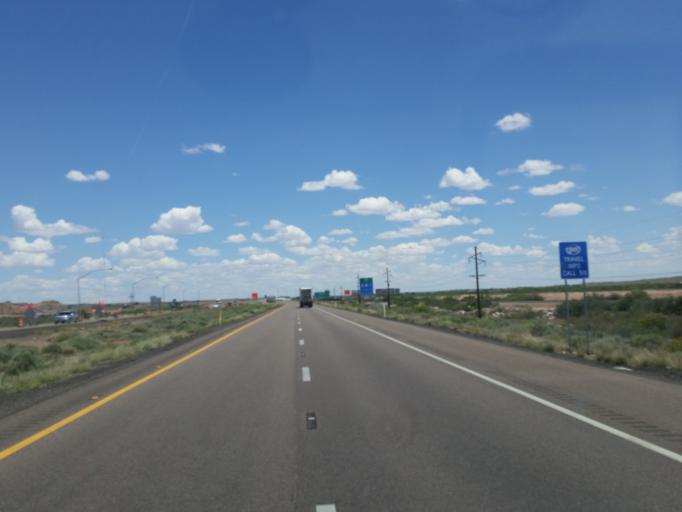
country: US
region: Arizona
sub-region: Navajo County
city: Holbrook
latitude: 34.9054
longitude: -110.1969
